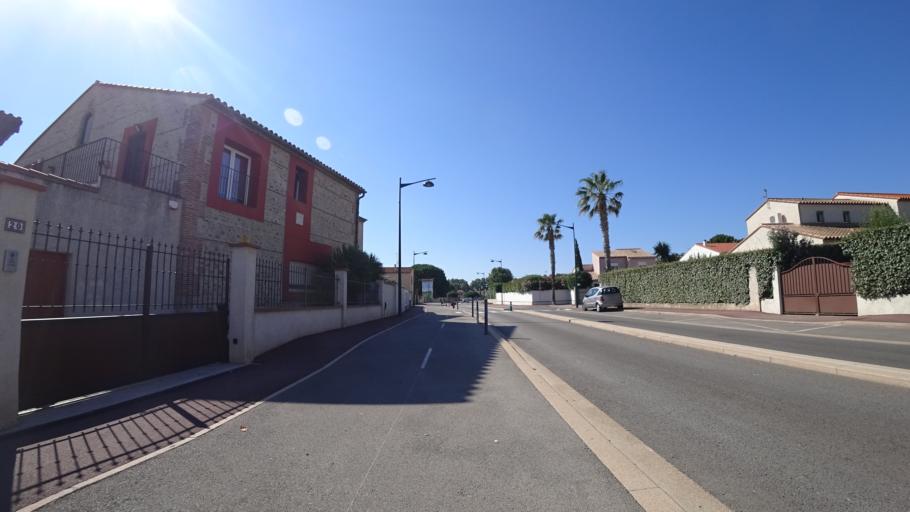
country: FR
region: Languedoc-Roussillon
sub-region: Departement des Pyrenees-Orientales
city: Bompas
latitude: 42.7248
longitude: 2.9370
